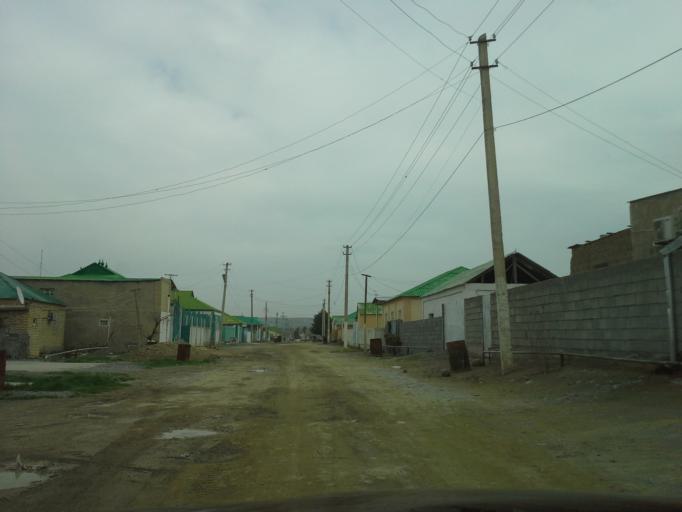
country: TM
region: Ahal
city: Abadan
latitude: 37.9772
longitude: 58.2192
